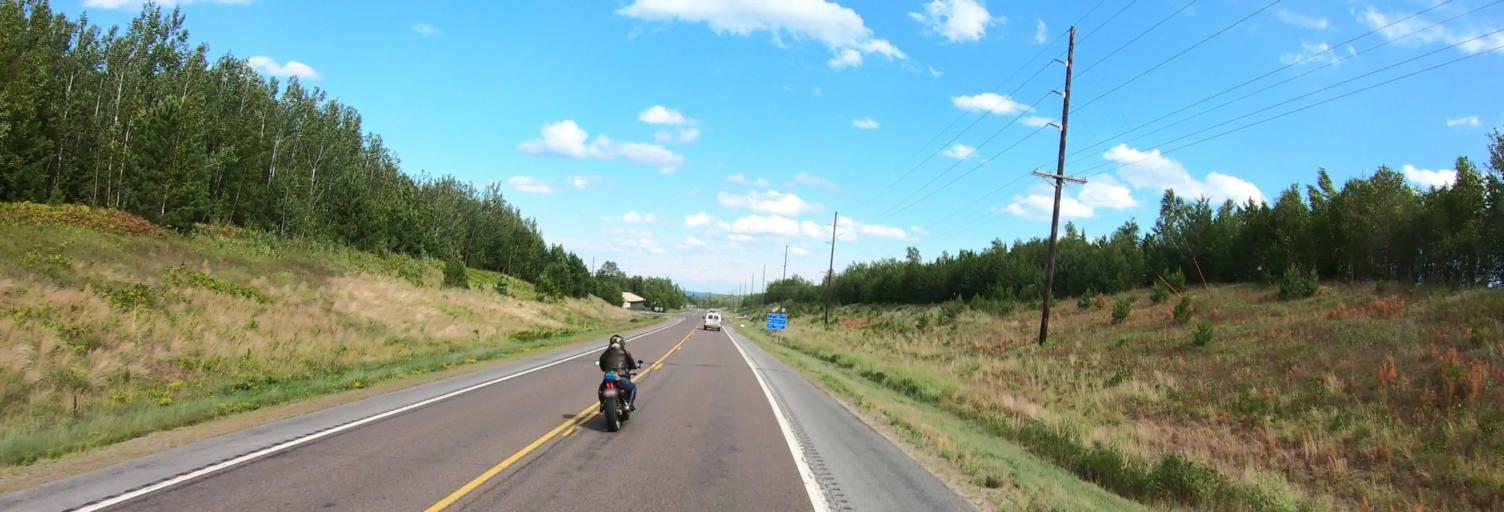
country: US
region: Minnesota
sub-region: Saint Louis County
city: Virginia
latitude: 47.8528
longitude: -92.4196
